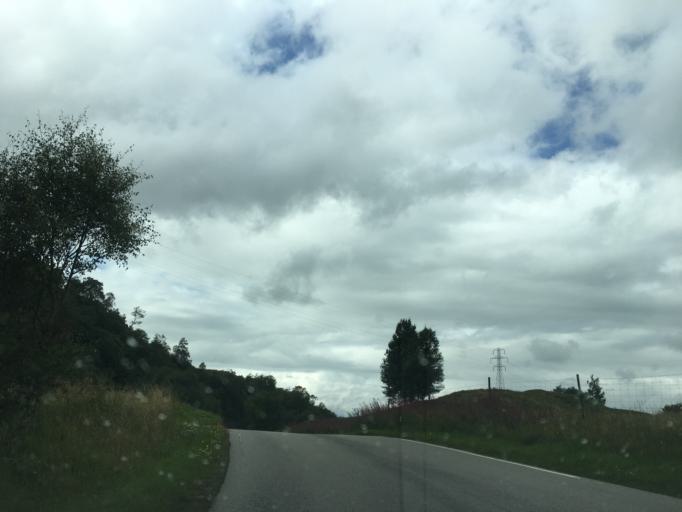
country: GB
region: Scotland
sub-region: Argyll and Bute
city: Oban
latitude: 56.3884
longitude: -5.1928
